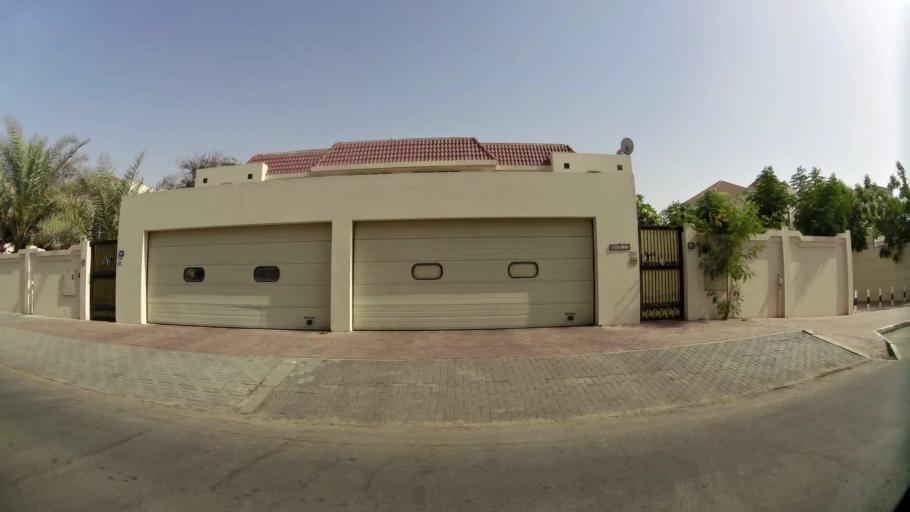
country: AE
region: Ash Shariqah
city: Sharjah
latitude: 25.2384
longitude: 55.3545
